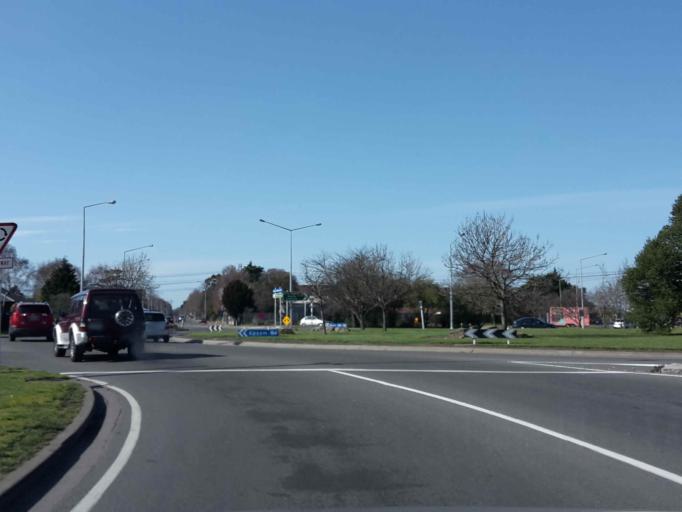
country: NZ
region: Canterbury
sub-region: Selwyn District
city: Prebbleton
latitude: -43.5394
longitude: 172.5533
